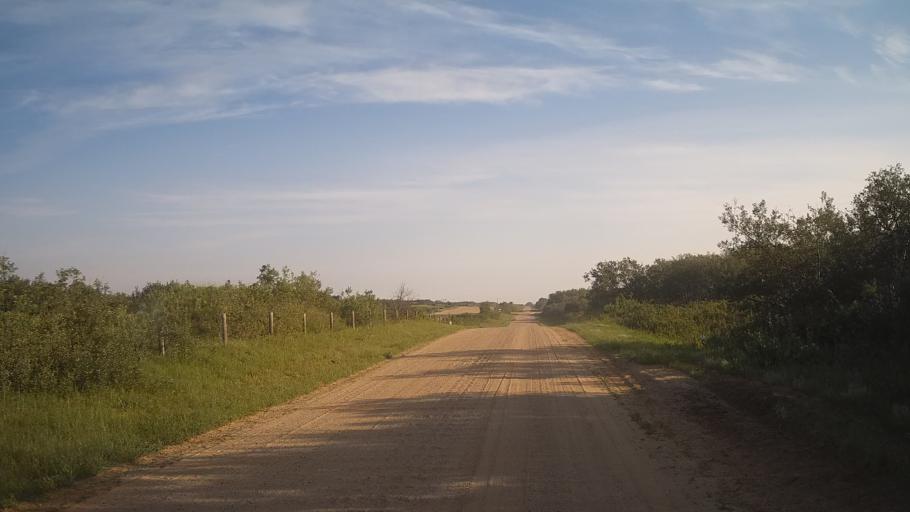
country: CA
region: Saskatchewan
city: Saskatoon
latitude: 51.8487
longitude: -106.5238
